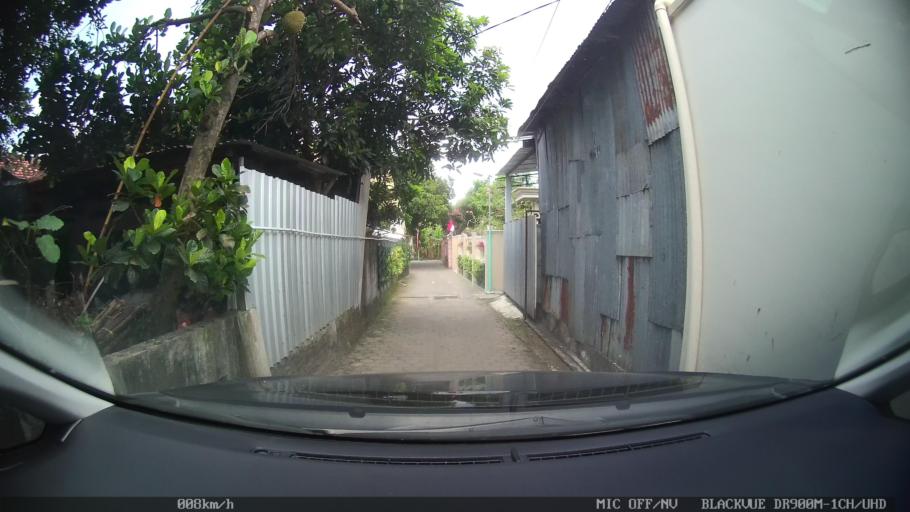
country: ID
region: Daerah Istimewa Yogyakarta
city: Yogyakarta
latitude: -7.8161
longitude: 110.3986
